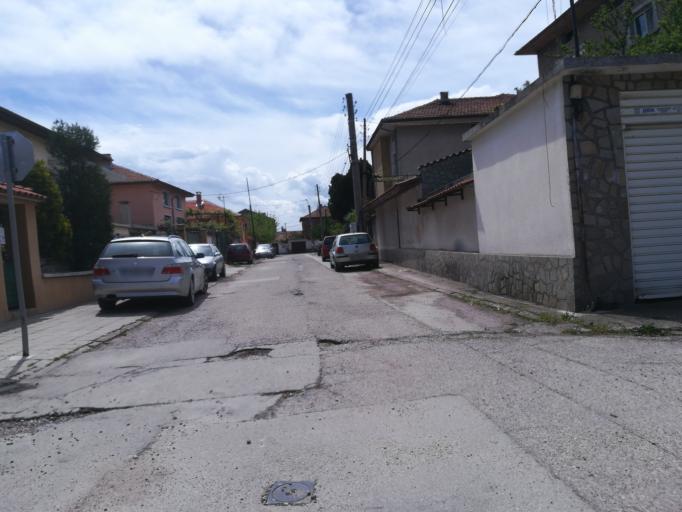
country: BG
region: Stara Zagora
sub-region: Obshtina Chirpan
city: Chirpan
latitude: 42.0949
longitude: 25.2249
